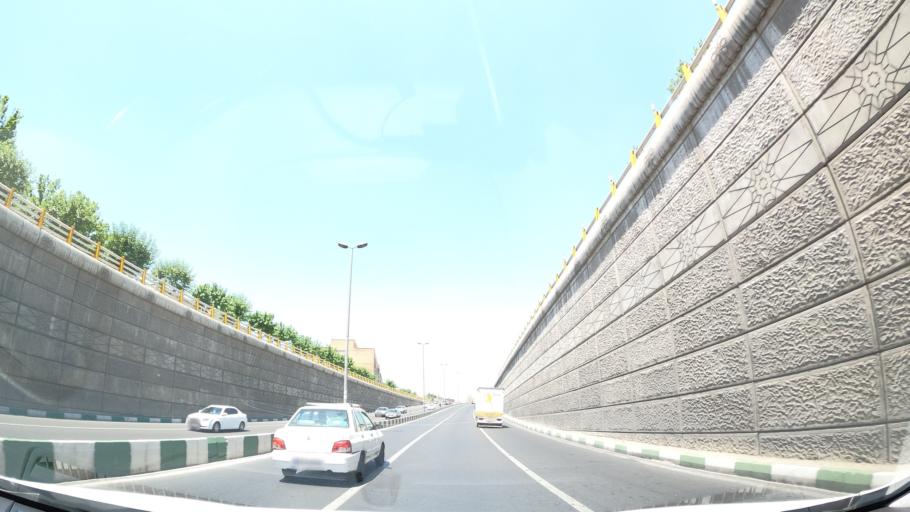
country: IR
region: Tehran
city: Tehran
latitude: 35.7232
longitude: 51.3882
